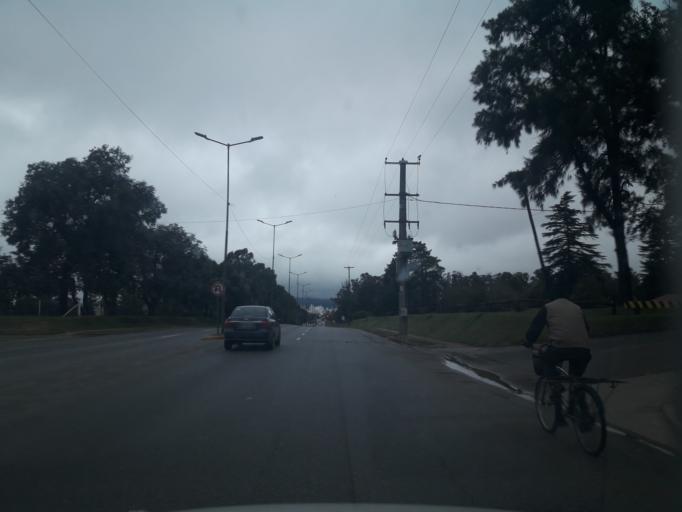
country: AR
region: Buenos Aires
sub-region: Partido de Tandil
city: Tandil
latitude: -37.3063
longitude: -59.1629
